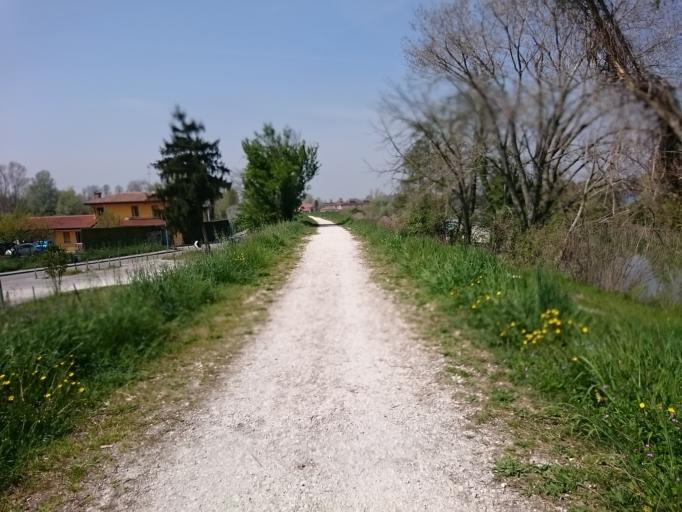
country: IT
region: Veneto
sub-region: Provincia di Padova
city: Mandriola-Sant'Agostino
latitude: 45.3878
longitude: 11.8482
